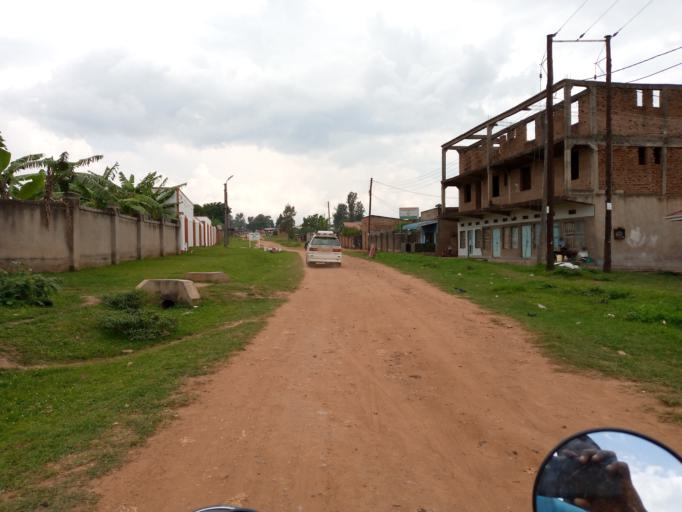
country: UG
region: Eastern Region
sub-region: Mbale District
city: Mbale
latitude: 1.0871
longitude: 34.1699
